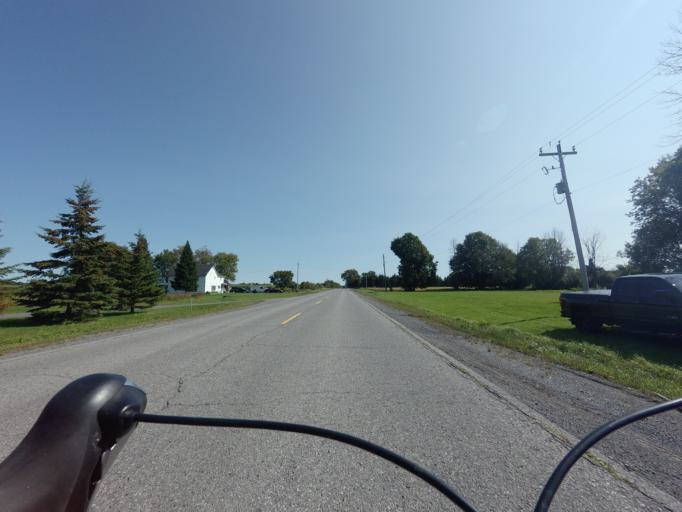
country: CA
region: Ontario
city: Carleton Place
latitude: 45.3452
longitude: -76.1064
